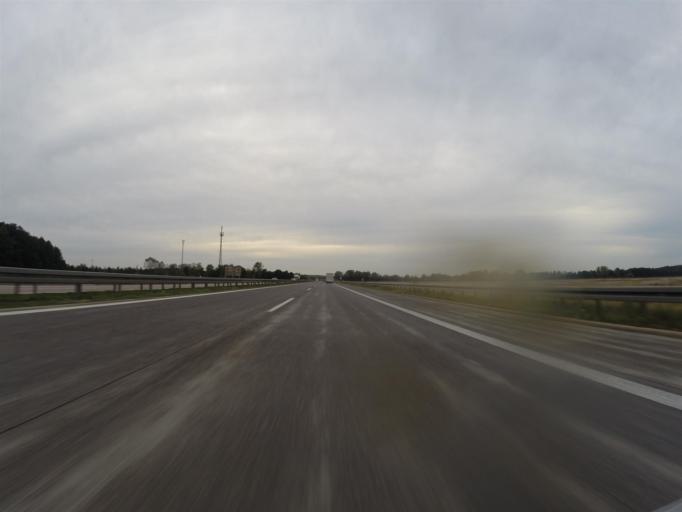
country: DE
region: Saxony
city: Naunhof
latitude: 51.2833
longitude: 12.6491
